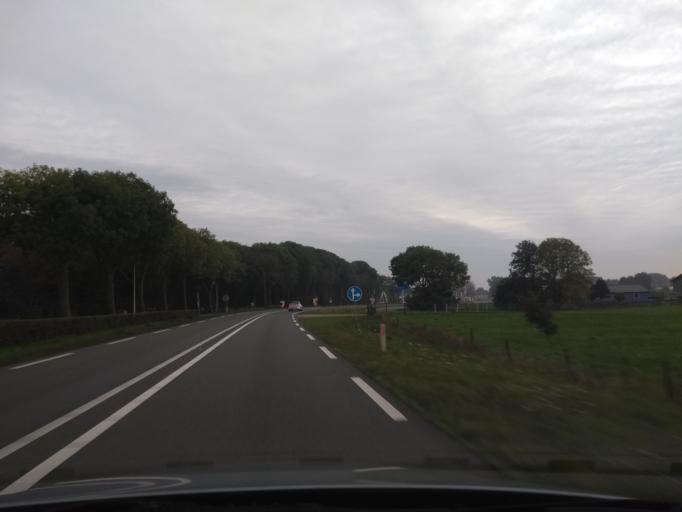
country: NL
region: Overijssel
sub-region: Gemeente Zwartewaterland
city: Hasselt
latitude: 52.5975
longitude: 6.0961
